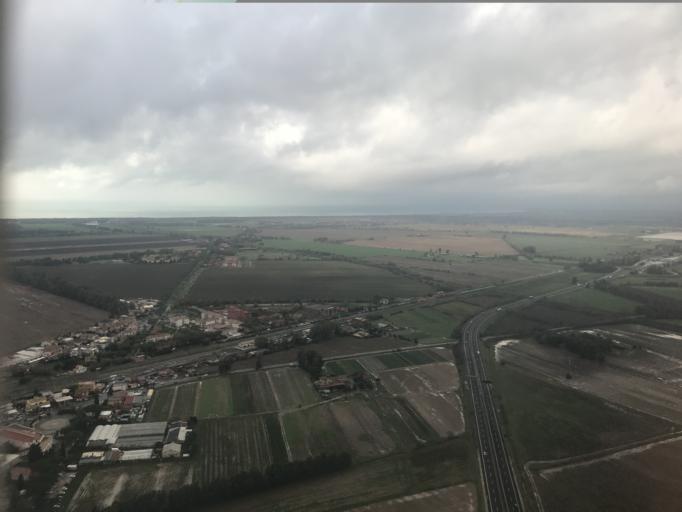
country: IT
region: Latium
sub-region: Citta metropolitana di Roma Capitale
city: Maccarese
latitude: 41.8790
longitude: 12.2481
